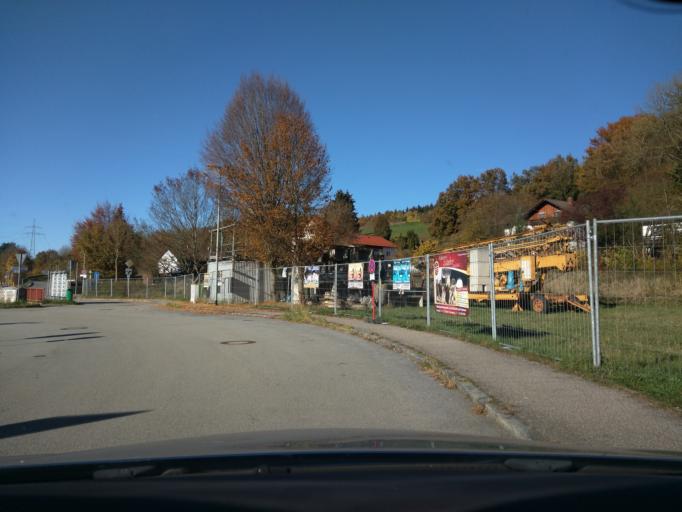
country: DE
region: Bavaria
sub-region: Lower Bavaria
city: Passau
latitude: 48.5821
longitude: 13.4100
